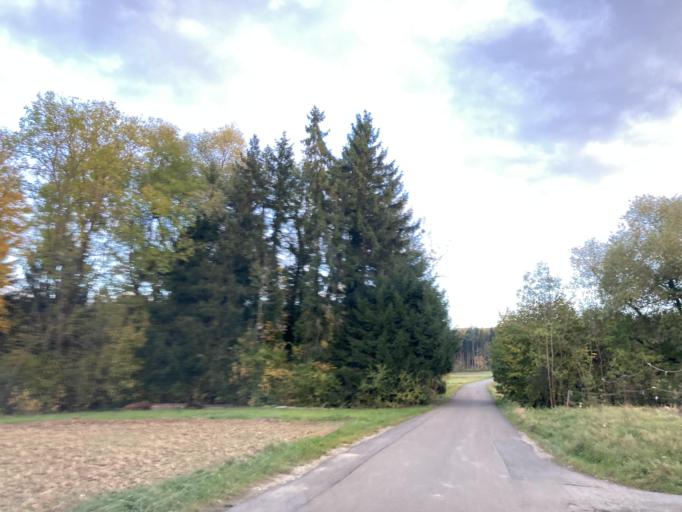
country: DE
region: Baden-Wuerttemberg
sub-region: Tuebingen Region
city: Gomaringen
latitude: 48.4416
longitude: 9.1046
